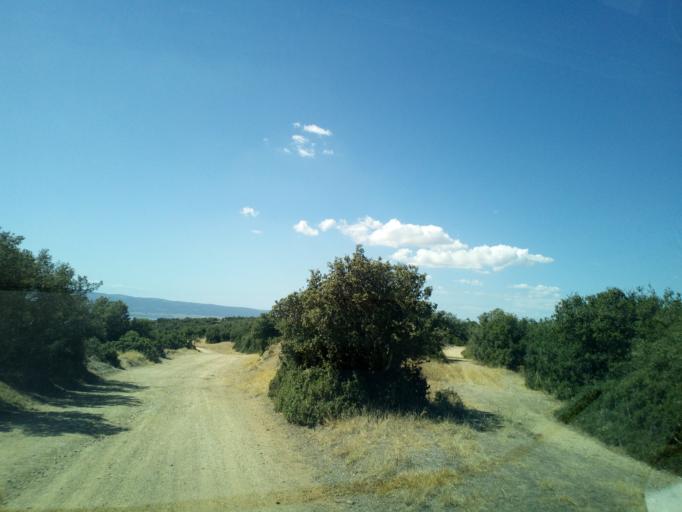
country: GR
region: Central Macedonia
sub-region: Nomos Thessalonikis
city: Gerakarou
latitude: 40.7185
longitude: 23.2180
